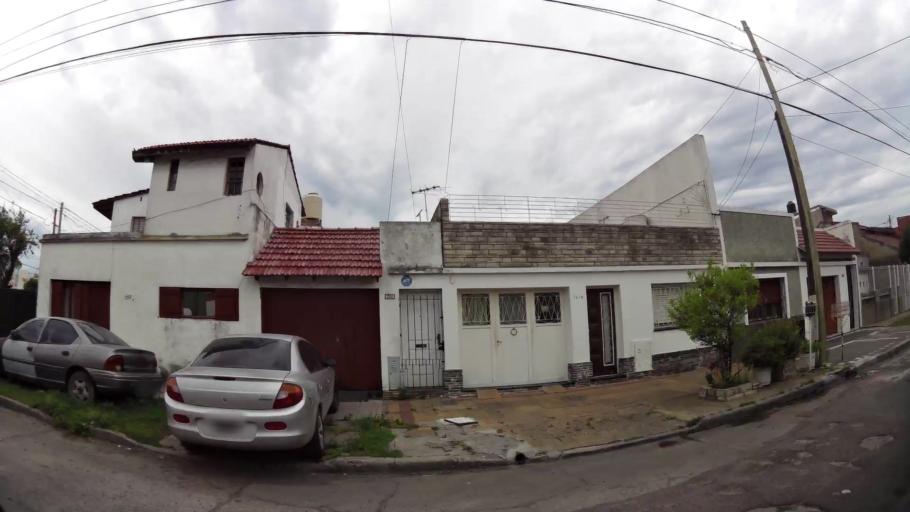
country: AR
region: Buenos Aires
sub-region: Partido de Lanus
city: Lanus
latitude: -34.6836
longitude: -58.3969
